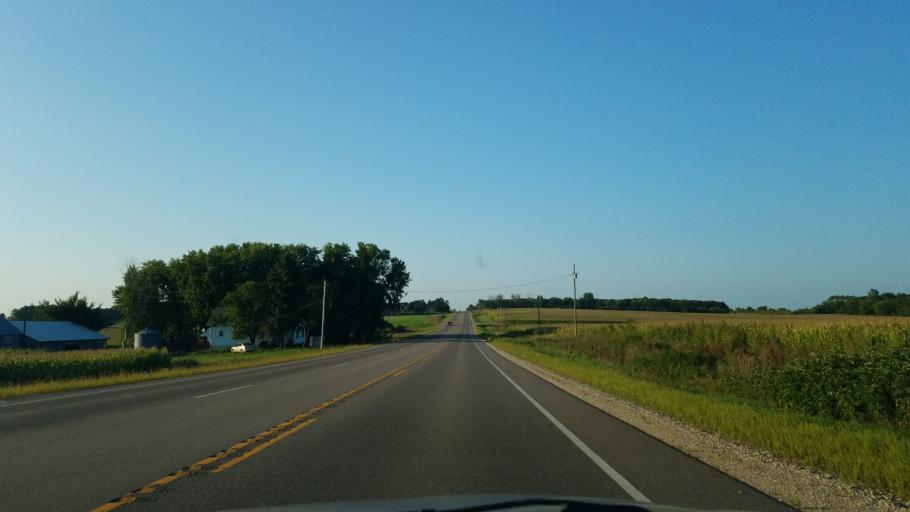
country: US
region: Wisconsin
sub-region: Saint Croix County
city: Baldwin
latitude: 45.1047
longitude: -92.3754
